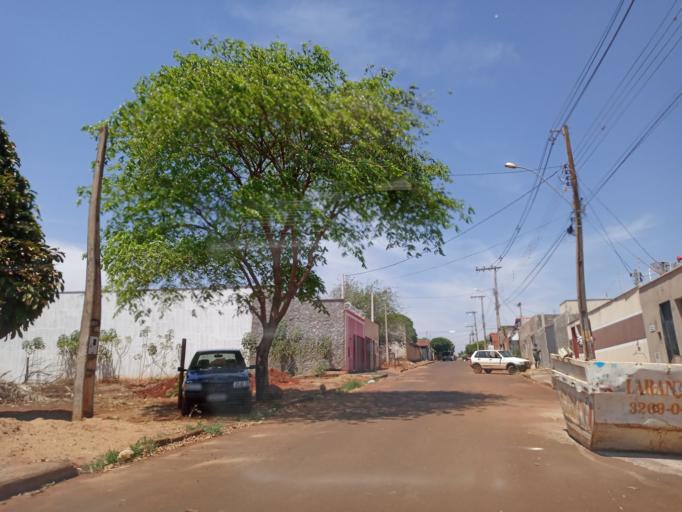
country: BR
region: Minas Gerais
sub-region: Ituiutaba
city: Ituiutaba
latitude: -18.9511
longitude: -49.4622
